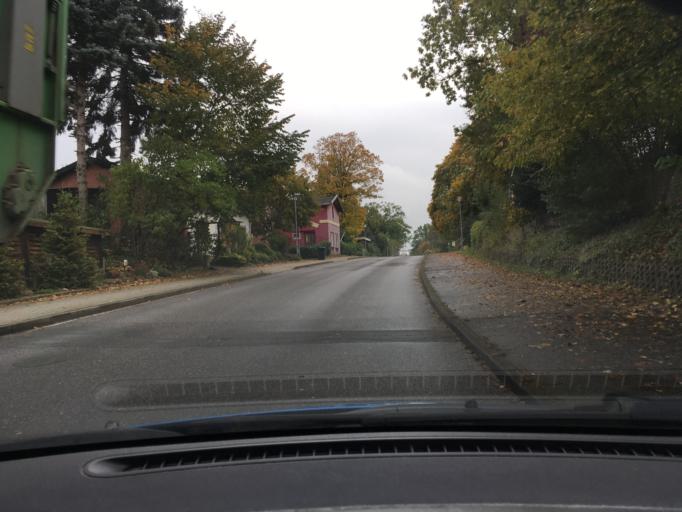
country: DE
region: Schleswig-Holstein
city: Klein Ronnau
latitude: 53.9719
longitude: 10.3129
